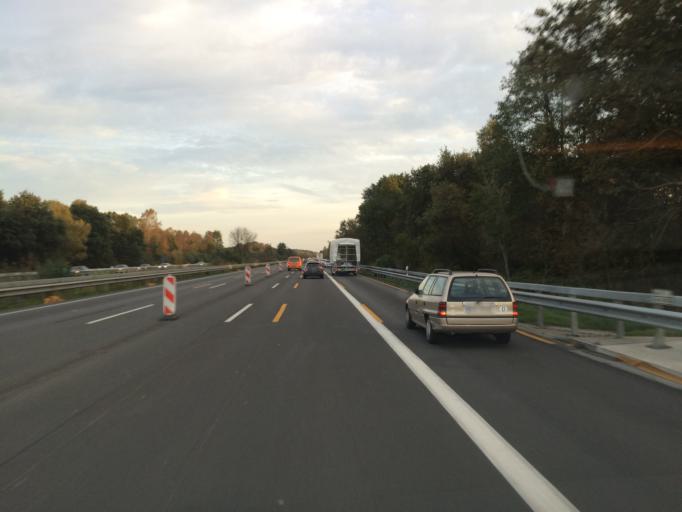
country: DE
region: Lower Saxony
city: Hademstorf
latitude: 52.7387
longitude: 9.6714
